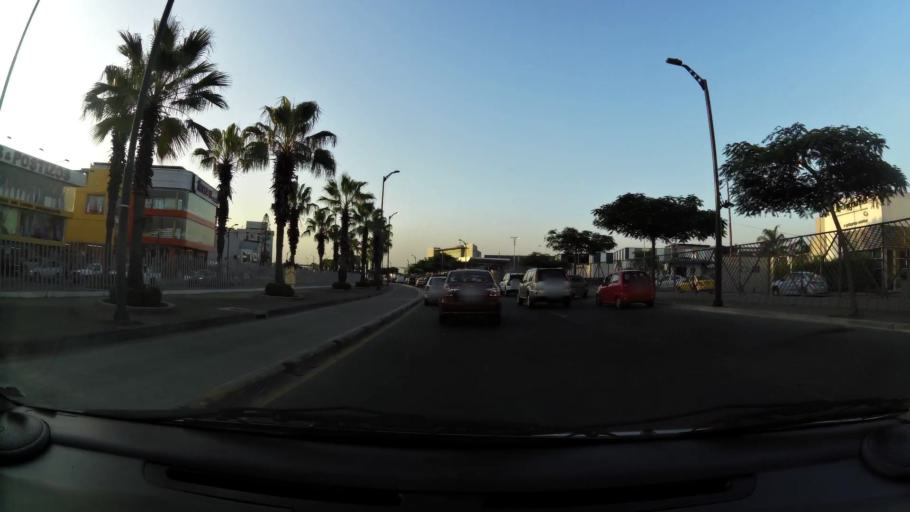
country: EC
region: Guayas
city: Eloy Alfaro
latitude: -2.1544
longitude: -79.8860
